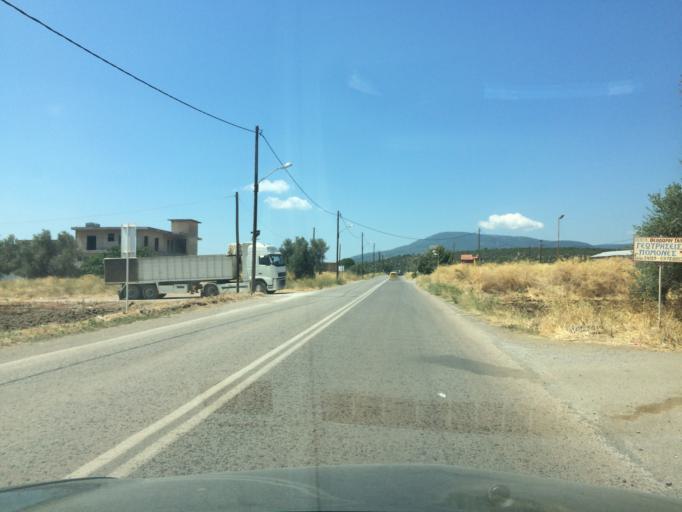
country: GR
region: Central Greece
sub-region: Nomos Evvoias
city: Psachna
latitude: 38.5784
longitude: 23.6280
